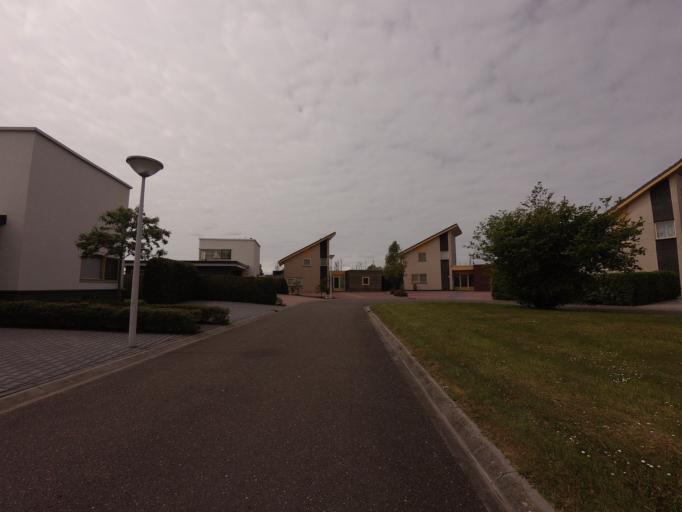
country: NL
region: Friesland
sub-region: Sudwest Fryslan
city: Koudum
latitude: 52.9014
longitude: 5.4665
